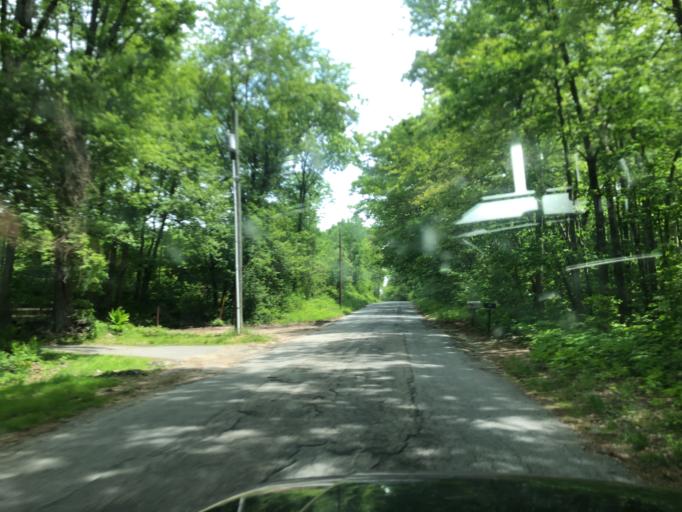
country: US
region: Connecticut
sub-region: Windham County
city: Thompson
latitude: 41.9634
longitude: -71.8531
